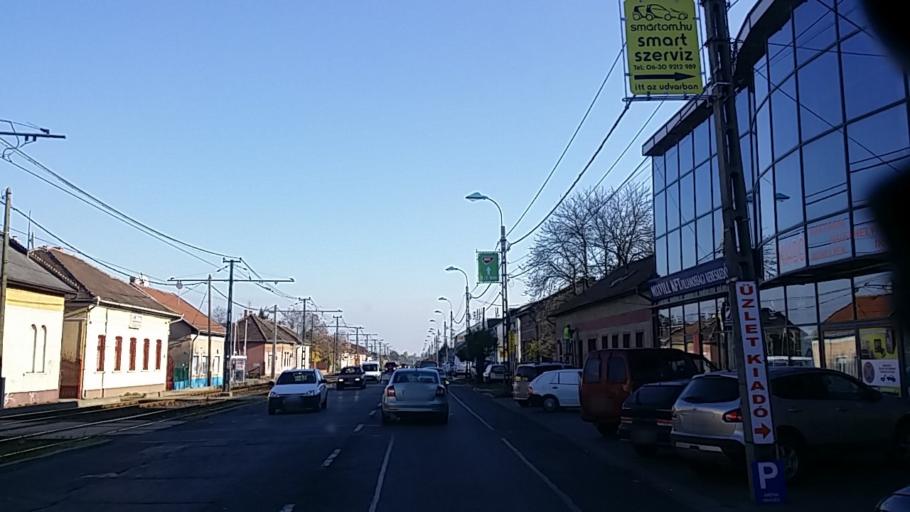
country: HU
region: Budapest
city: Budapest XVIII. keruelet
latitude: 47.4387
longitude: 19.1898
